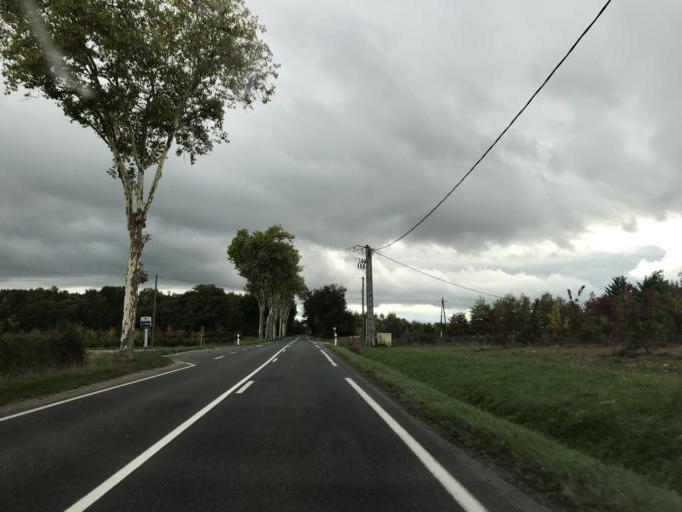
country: FR
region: Rhone-Alpes
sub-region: Departement de l'Ain
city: Saint-Trivier-sur-Moignans
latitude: 46.0888
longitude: 4.9171
